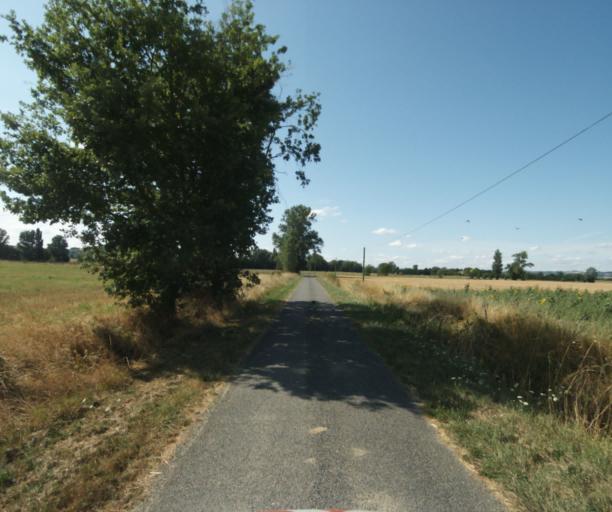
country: FR
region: Midi-Pyrenees
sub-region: Departement de la Haute-Garonne
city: Revel
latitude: 43.5016
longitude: 1.9694
